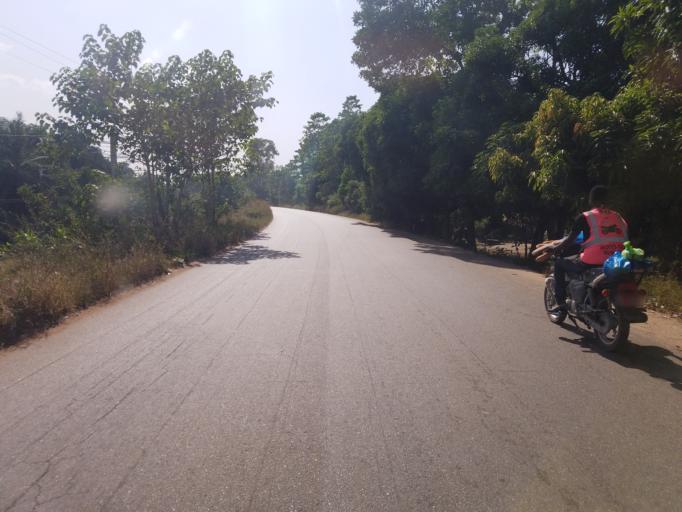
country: GN
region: Boke
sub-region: Fria
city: Fria
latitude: 10.0808
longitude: -13.6979
